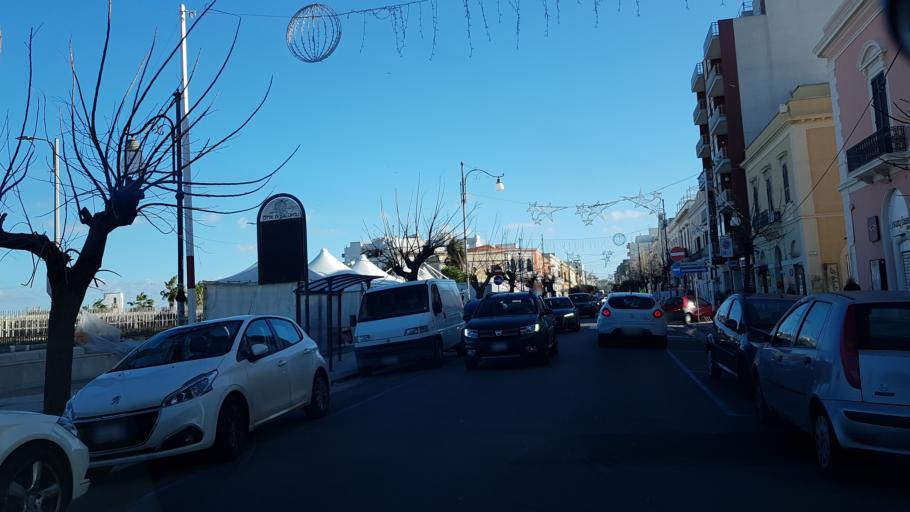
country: IT
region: Apulia
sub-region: Provincia di Lecce
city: Gallipoli
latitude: 40.0562
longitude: 17.9829
